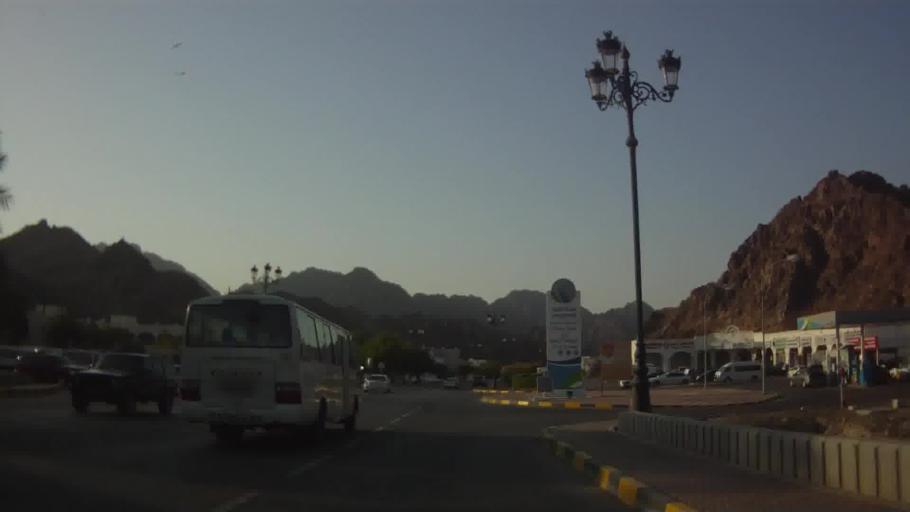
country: OM
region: Muhafazat Masqat
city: Muscat
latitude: 23.5897
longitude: 58.5997
